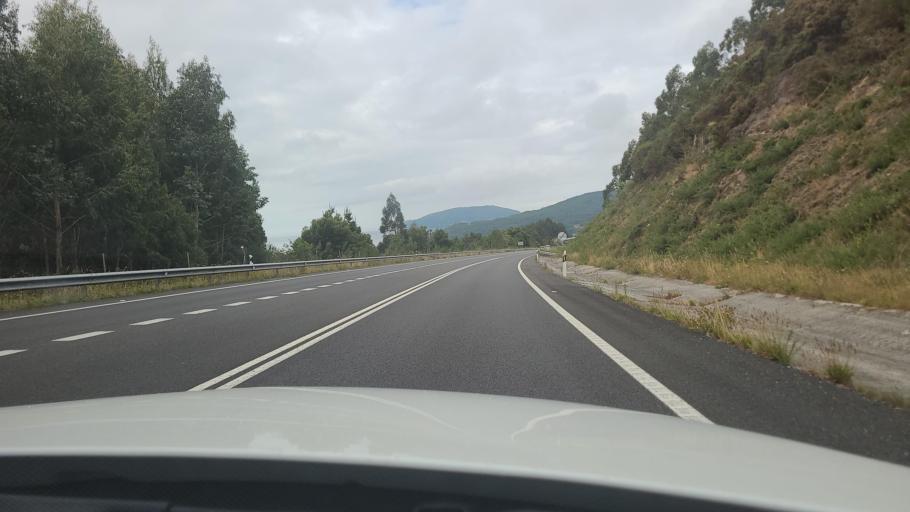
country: ES
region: Galicia
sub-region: Provincia da Coruna
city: Corcubion
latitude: 42.9541
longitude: -9.2122
